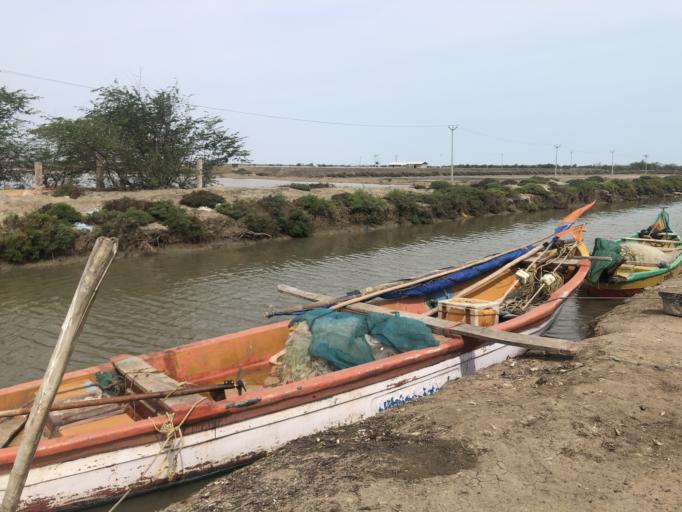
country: IN
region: Tamil Nadu
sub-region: Thanjavur
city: Adirampattinam
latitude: 10.3218
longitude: 79.3791
